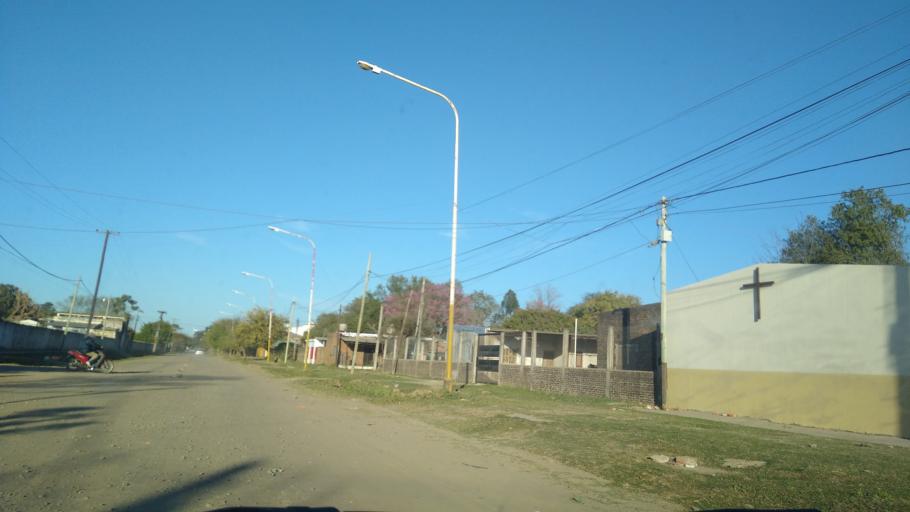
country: AR
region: Chaco
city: Barranqueras
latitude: -27.4789
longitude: -58.9461
